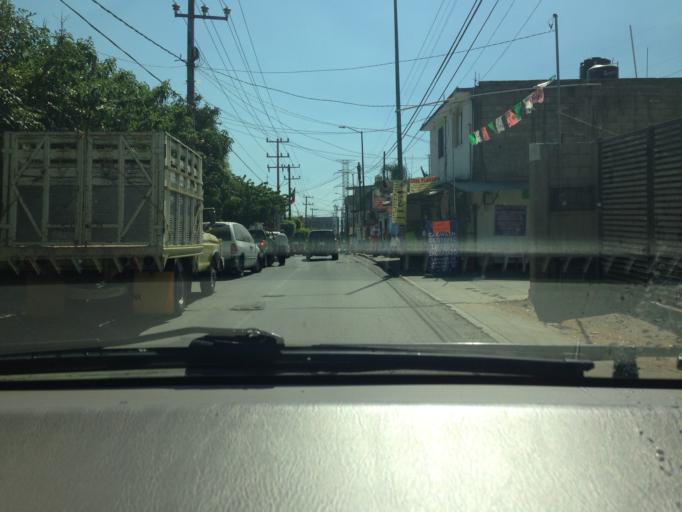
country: MX
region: Morelos
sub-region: Cuernavaca
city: Fraccionamiento Lomas de Ahuatlan
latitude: 18.9657
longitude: -99.2277
